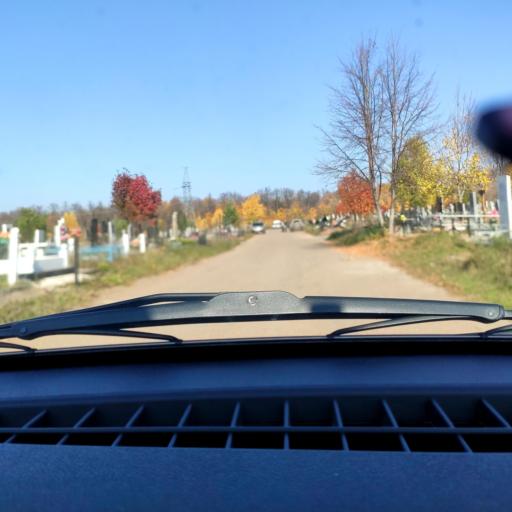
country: RU
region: Bashkortostan
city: Mikhaylovka
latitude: 54.8166
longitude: 55.8665
